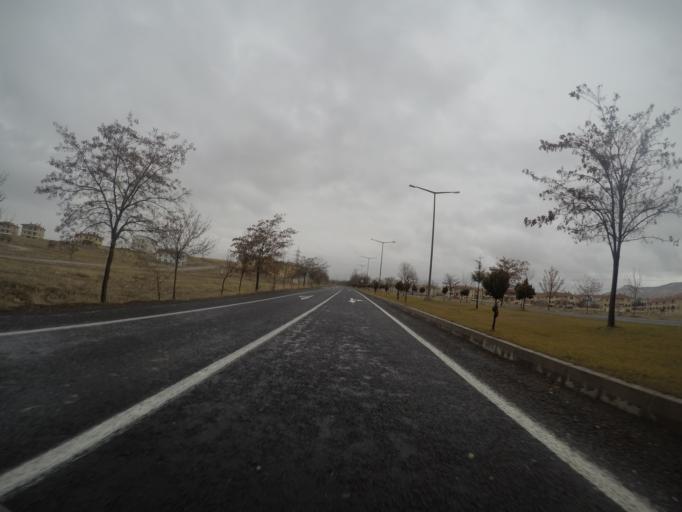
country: TR
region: Nevsehir
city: Avanos
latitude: 38.7009
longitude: 34.8616
